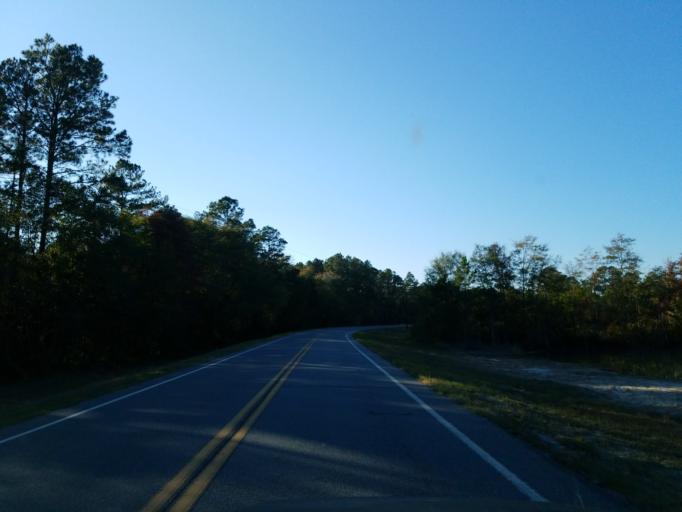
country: US
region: Georgia
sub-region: Lanier County
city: Lakeland
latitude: 30.9043
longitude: -83.0750
